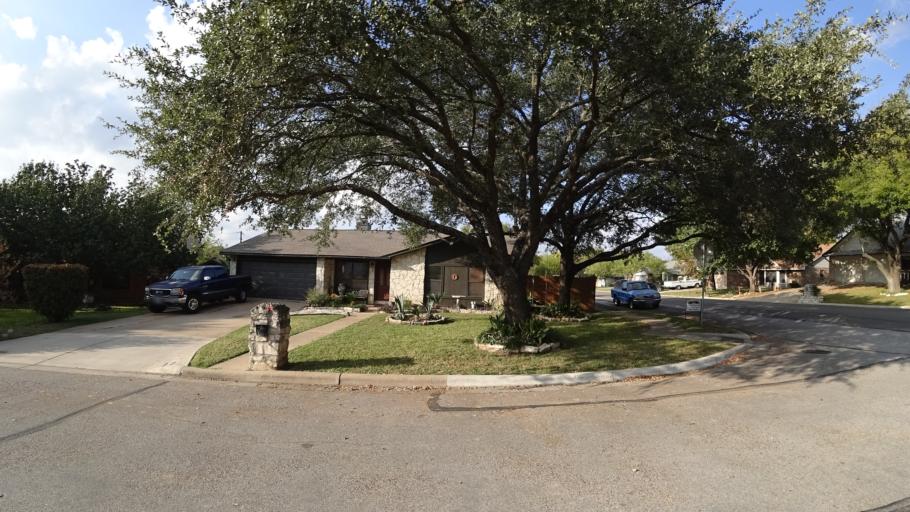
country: US
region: Texas
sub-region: Williamson County
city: Round Rock
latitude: 30.4912
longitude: -97.6661
